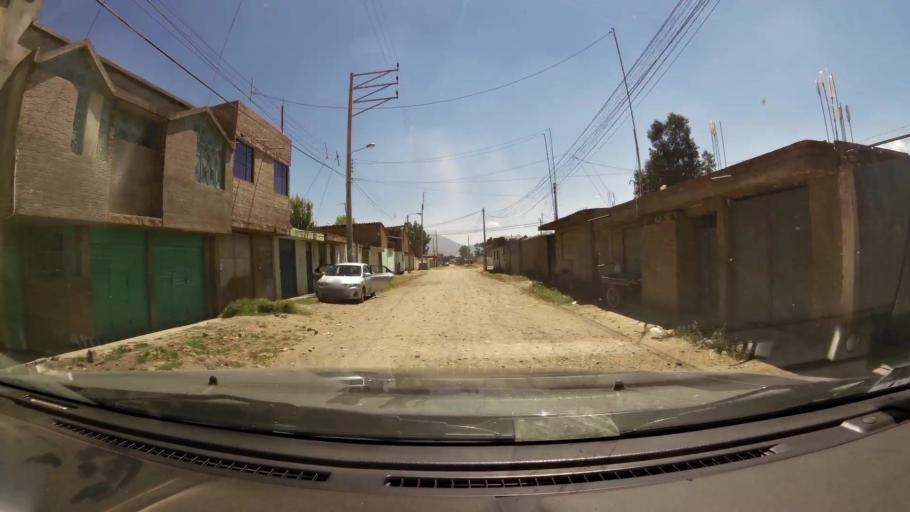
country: PE
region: Junin
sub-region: Provincia de Jauja
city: Jauja
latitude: -11.7744
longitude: -75.4914
